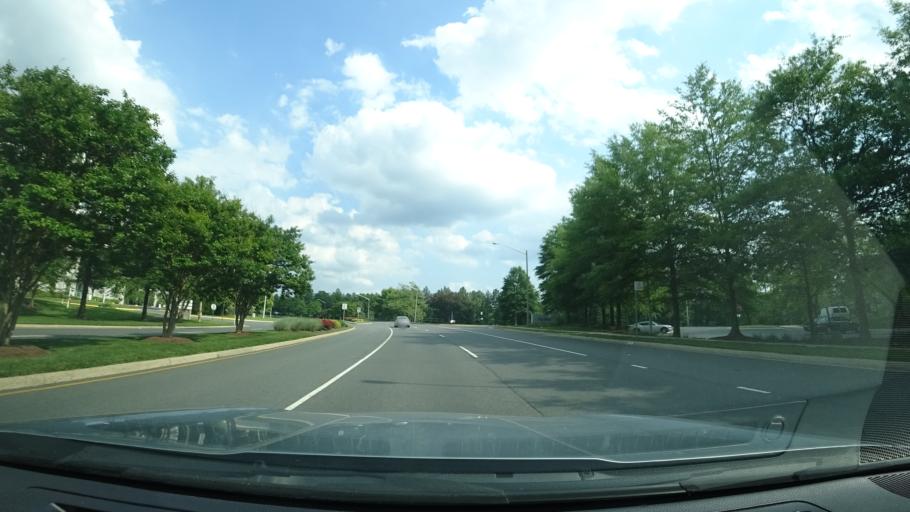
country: US
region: Virginia
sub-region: Fairfax County
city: Herndon
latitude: 38.9567
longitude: -77.3989
